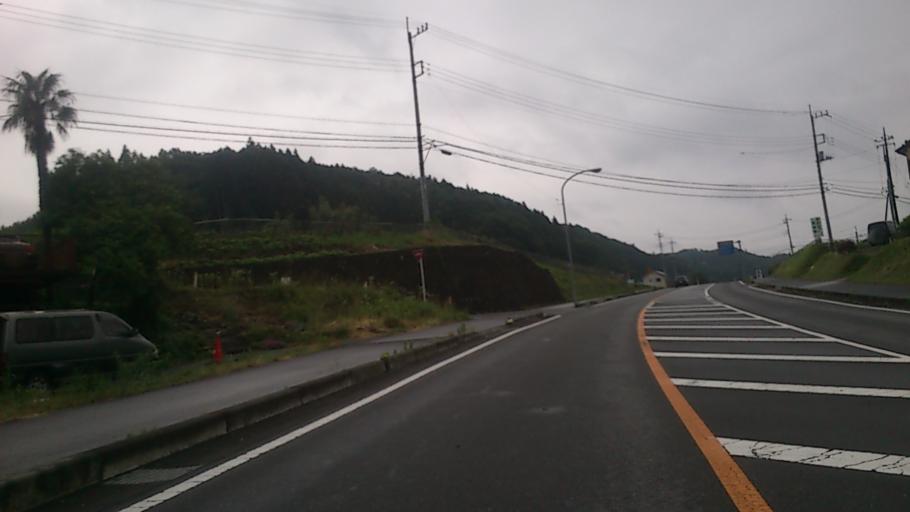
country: JP
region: Tochigi
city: Karasuyama
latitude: 36.7331
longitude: 140.1758
